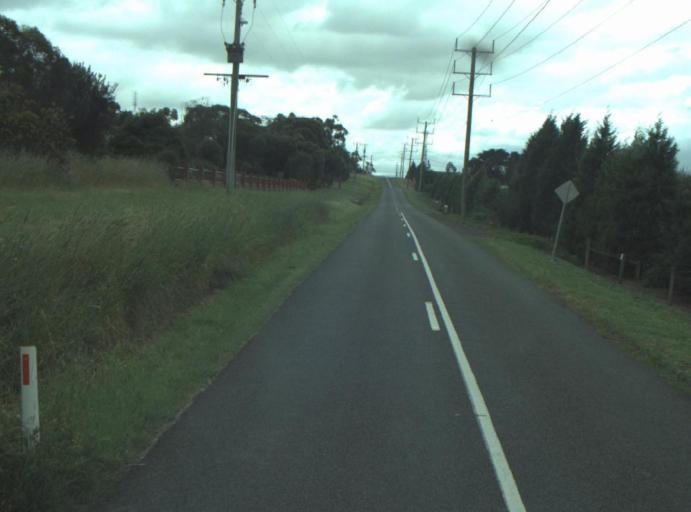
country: AU
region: Victoria
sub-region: Greater Geelong
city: Bell Post Hill
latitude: -38.0859
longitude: 144.3257
